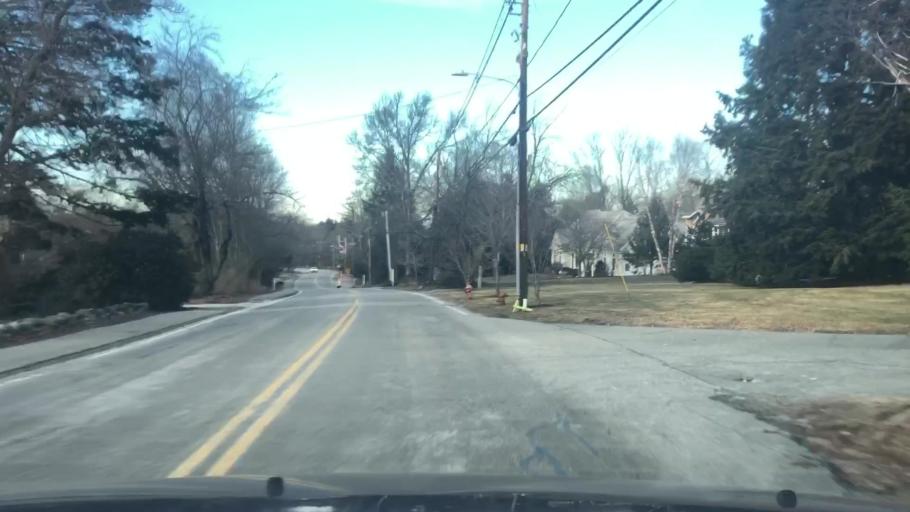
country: US
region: Massachusetts
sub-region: Essex County
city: Andover
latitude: 42.6769
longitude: -71.1151
